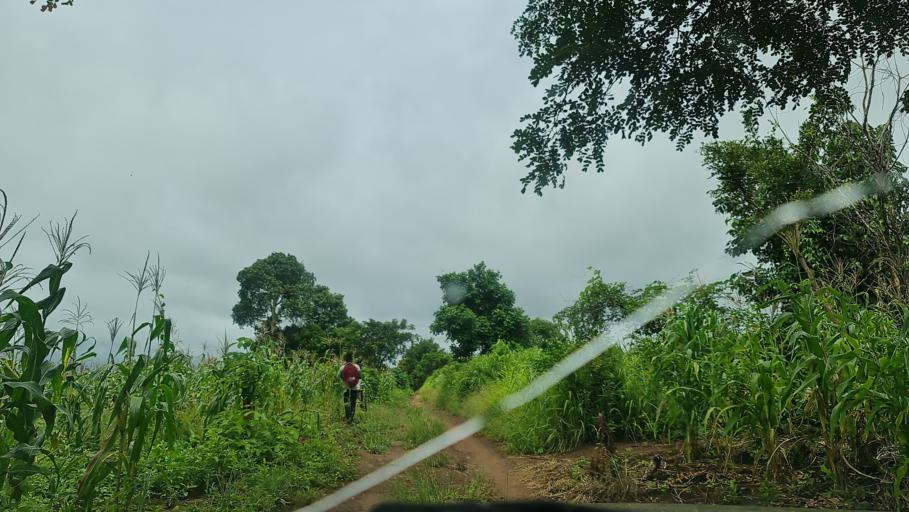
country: MW
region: Southern Region
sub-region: Nsanje District
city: Nsanje
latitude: -17.3825
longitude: 35.7774
